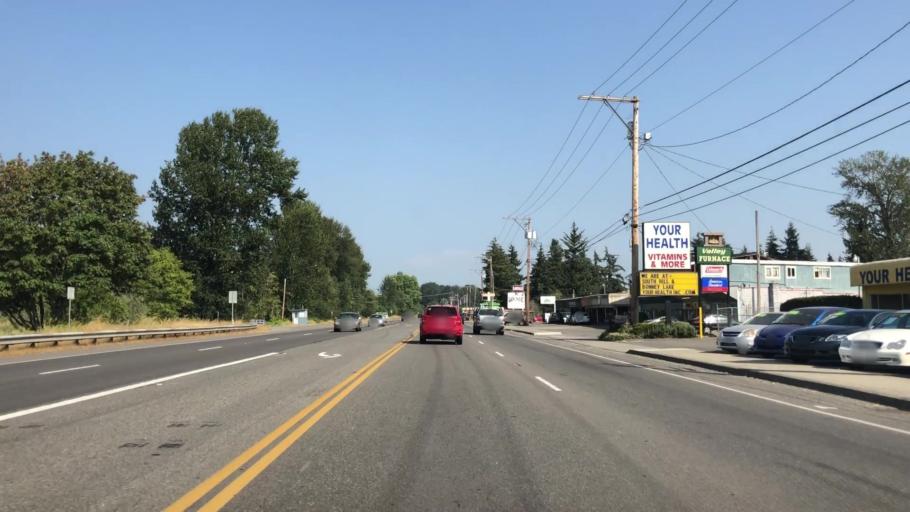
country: US
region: Washington
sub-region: Pierce County
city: Puyallup
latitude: 47.2077
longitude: -122.3254
